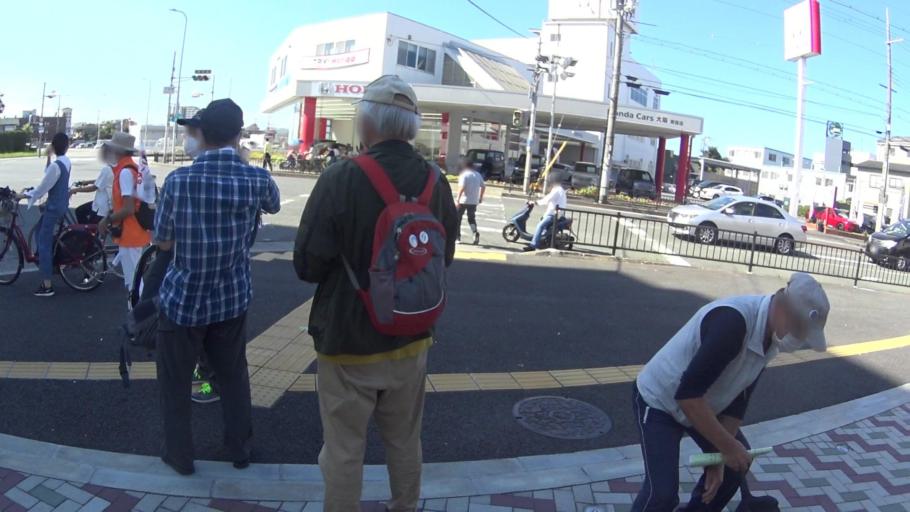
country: JP
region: Osaka
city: Takaishi
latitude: 34.5407
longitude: 135.4638
